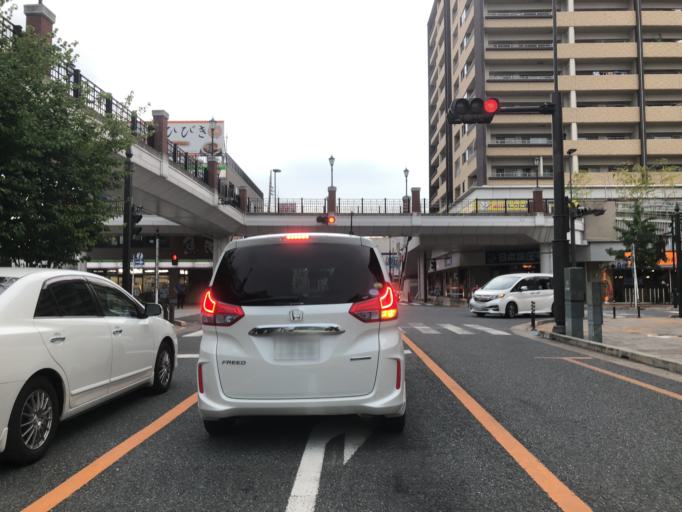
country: JP
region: Saitama
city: Sakado
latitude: 36.0352
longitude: 139.4021
